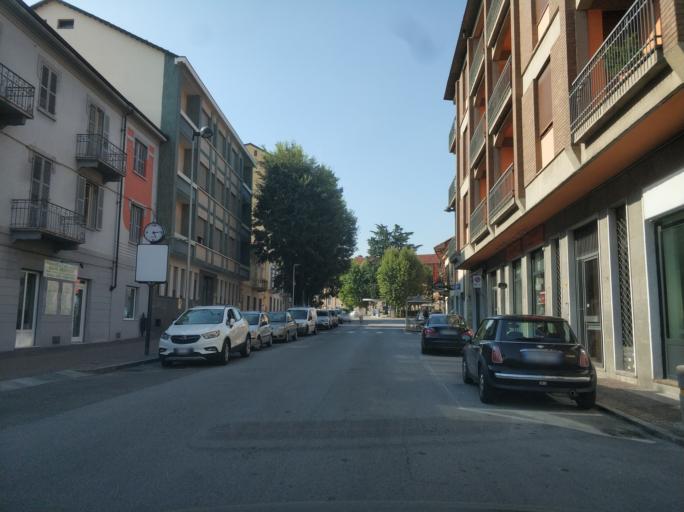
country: IT
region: Piedmont
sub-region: Provincia di Cuneo
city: Bra
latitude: 44.7004
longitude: 7.8484
